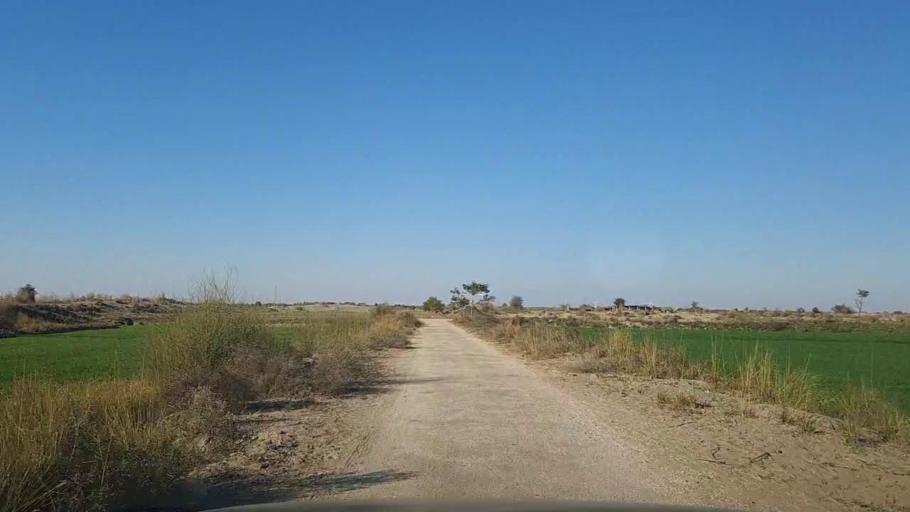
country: PK
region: Sindh
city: Khadro
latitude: 26.2549
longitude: 68.8674
